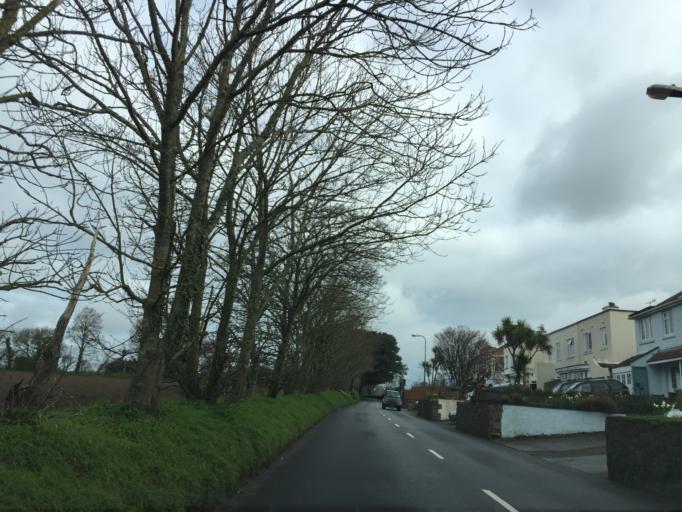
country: JE
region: St Helier
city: Saint Helier
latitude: 49.2091
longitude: -2.1425
